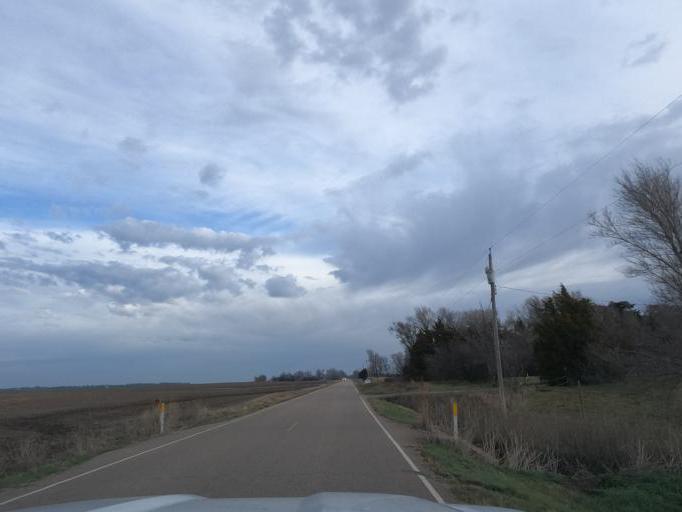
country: US
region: Kansas
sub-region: Reno County
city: South Hutchinson
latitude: 37.9756
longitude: -98.0874
